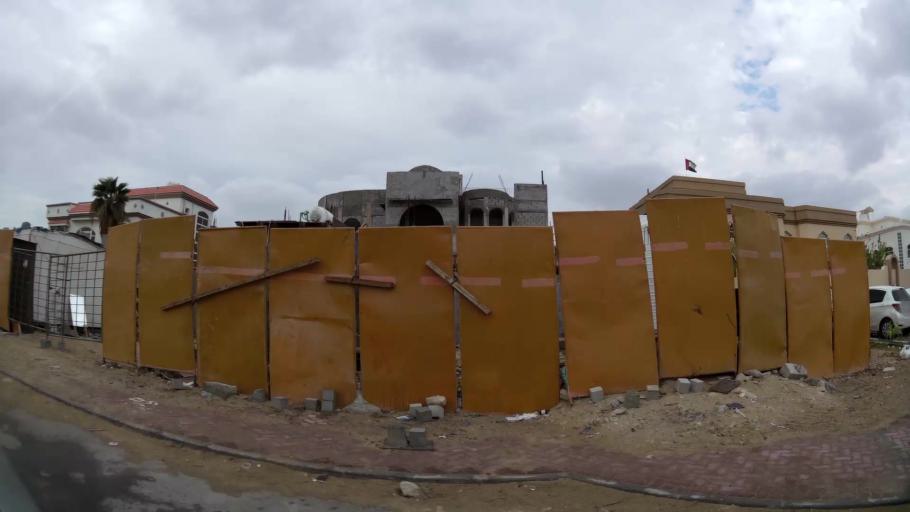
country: AE
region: Abu Dhabi
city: Abu Dhabi
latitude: 24.3541
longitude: 54.6289
